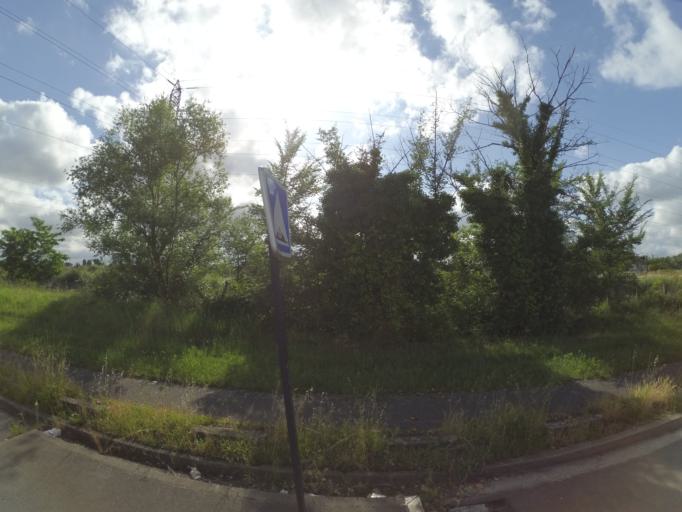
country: FR
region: Aquitaine
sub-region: Departement de la Gironde
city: Lormont
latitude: 44.8858
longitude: -0.5497
